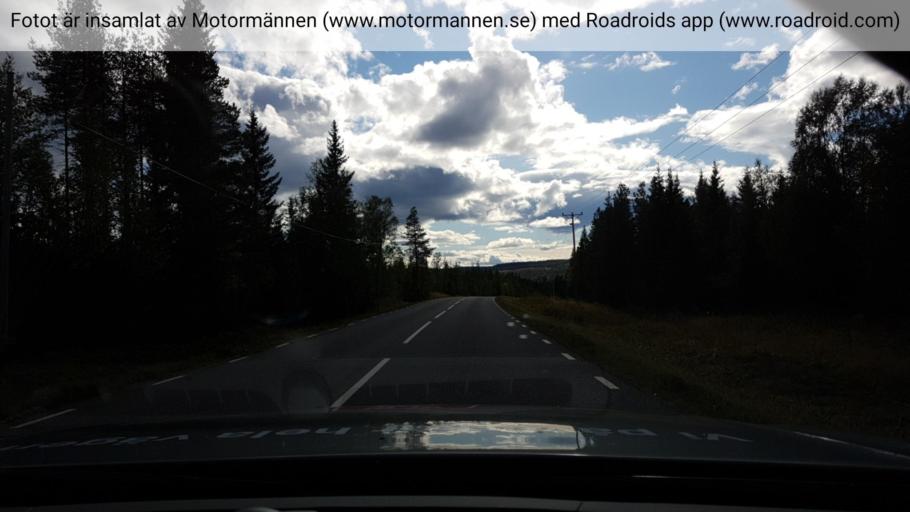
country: SE
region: Jaemtland
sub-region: Are Kommun
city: Jarpen
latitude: 63.4292
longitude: 13.3746
